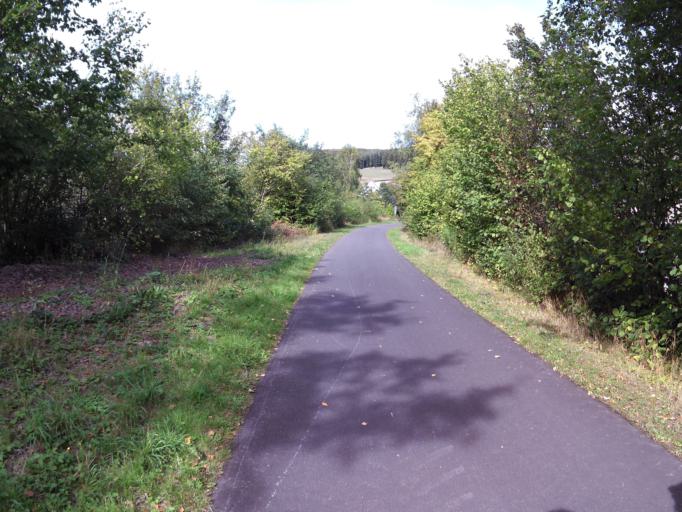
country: DE
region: Rheinland-Pfalz
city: Pronsfeld
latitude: 50.1588
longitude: 6.3324
